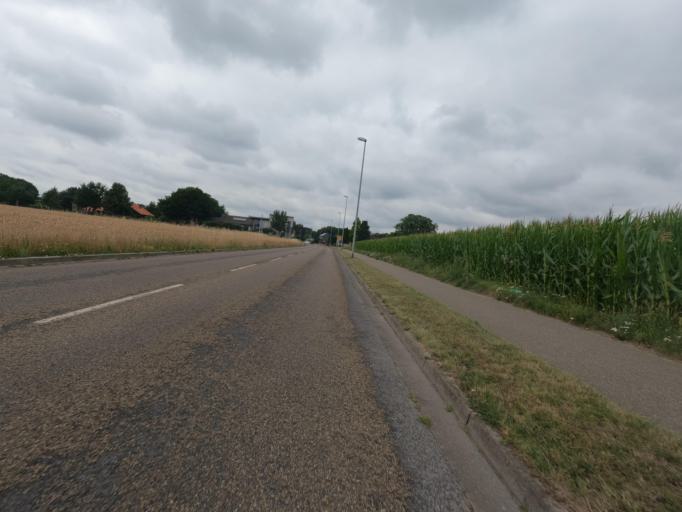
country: DE
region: North Rhine-Westphalia
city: Geilenkirchen
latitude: 50.9773
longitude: 6.1098
